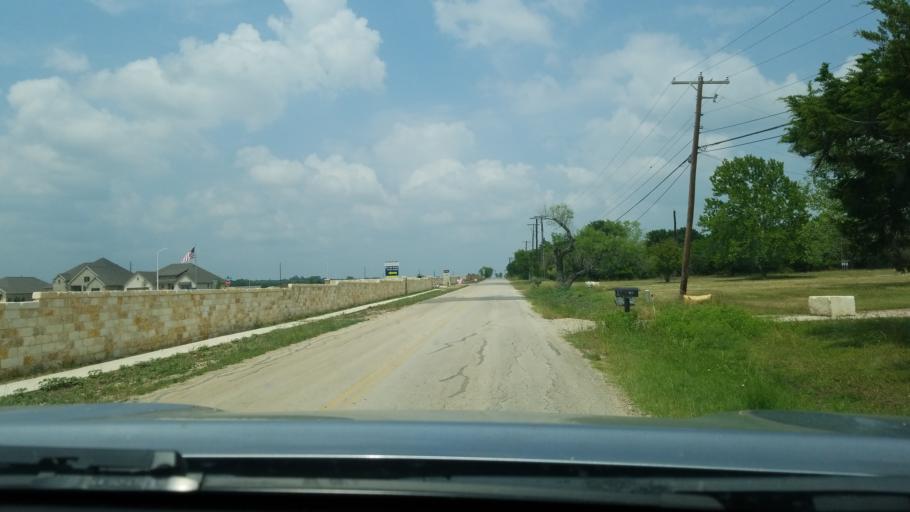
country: US
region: Texas
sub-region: Comal County
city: New Braunfels
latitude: 29.7459
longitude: -98.0955
